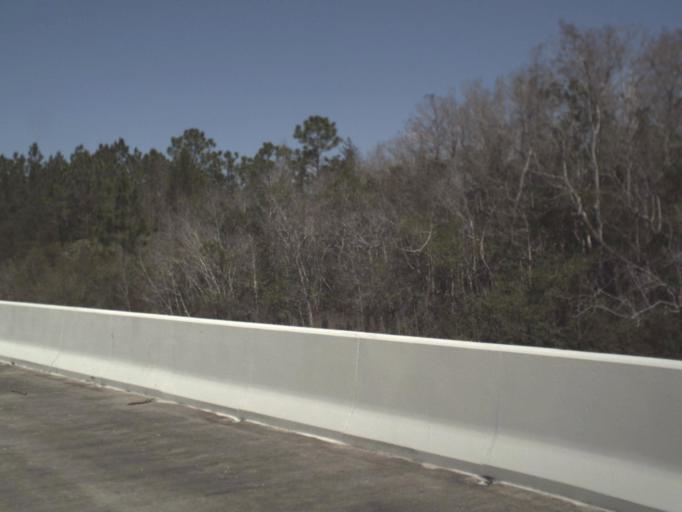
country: US
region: Florida
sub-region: Gulf County
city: Port Saint Joe
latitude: 29.7496
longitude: -85.2434
